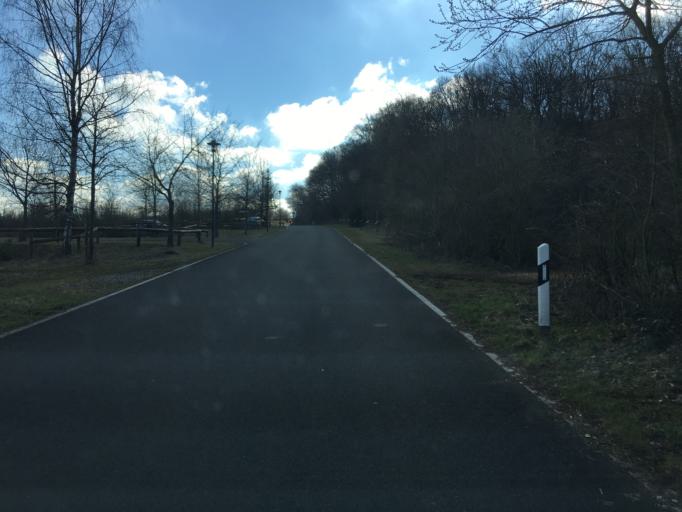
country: DE
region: North Rhine-Westphalia
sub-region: Regierungsbezirk Koln
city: Mechernich
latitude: 50.6173
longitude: 6.6297
